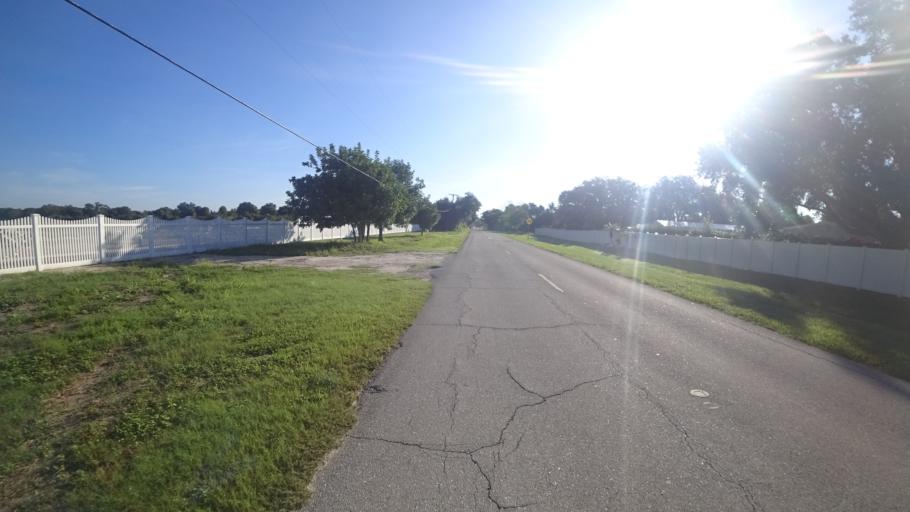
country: US
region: Florida
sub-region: Manatee County
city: Memphis
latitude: 27.5683
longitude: -82.5522
